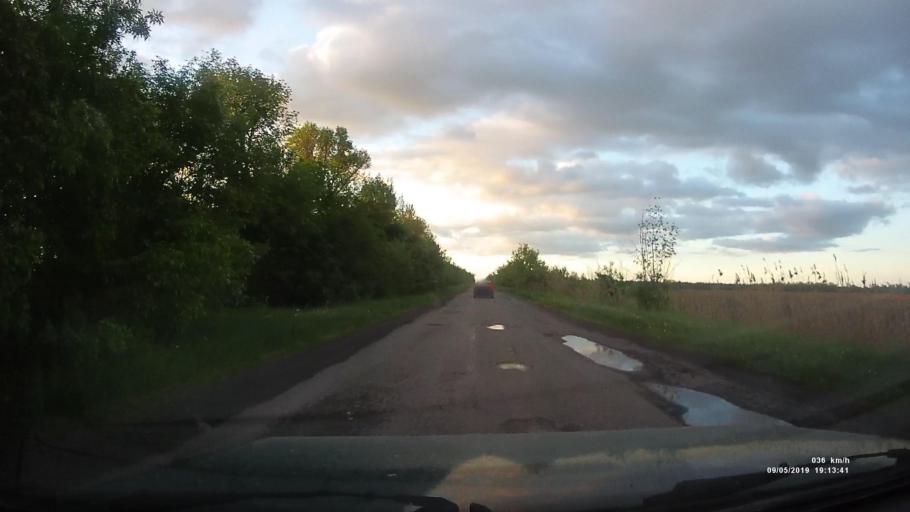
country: RU
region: Krasnodarskiy
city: Kanelovskaya
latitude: 46.7522
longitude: 39.2138
